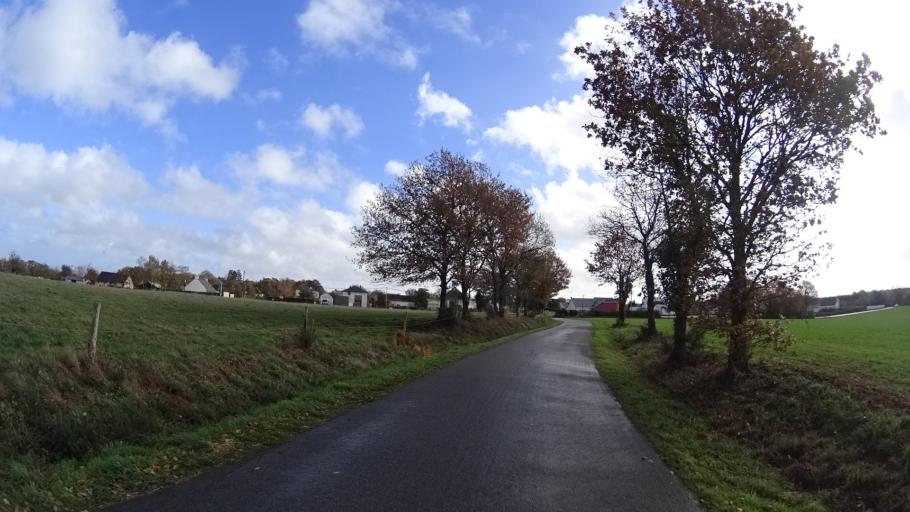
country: FR
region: Pays de la Loire
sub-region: Departement de la Loire-Atlantique
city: Saint-Nicolas-de-Redon
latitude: 47.6227
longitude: -2.0673
